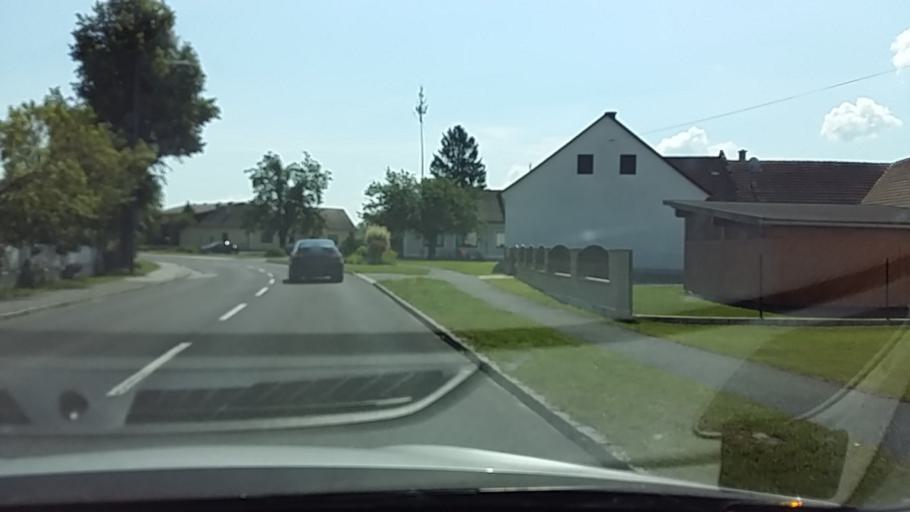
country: AT
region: Burgenland
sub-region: Politischer Bezirk Jennersdorf
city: Mogersdorf
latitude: 46.9479
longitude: 16.2332
